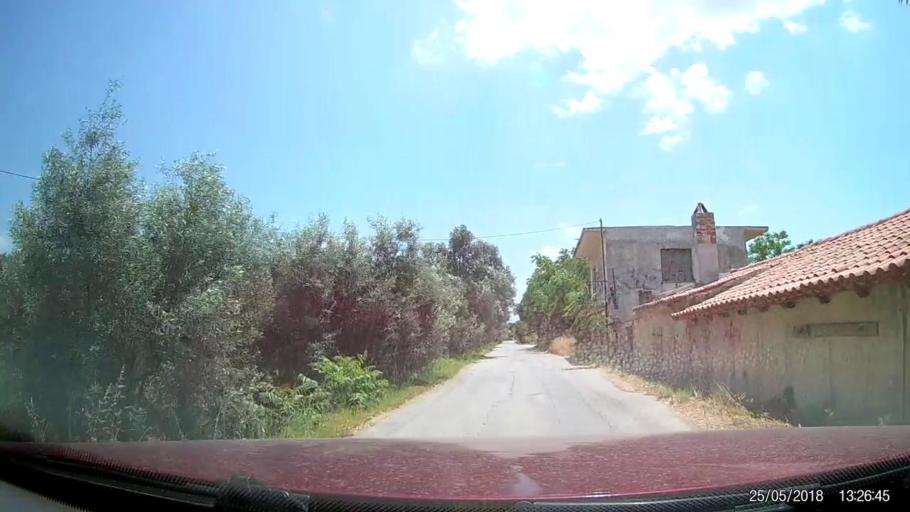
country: GR
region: Central Greece
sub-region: Nomos Evvoias
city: Mytikas
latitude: 38.4543
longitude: 23.6485
